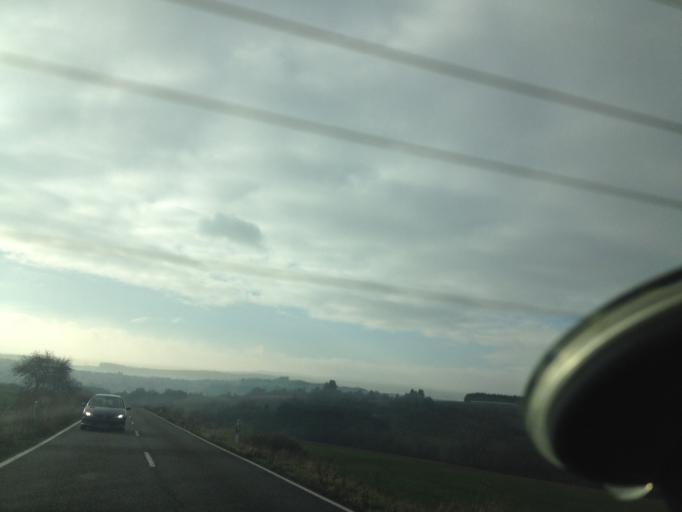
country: DE
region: Rheinland-Pfalz
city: Brucken
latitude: 49.4438
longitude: 7.3722
